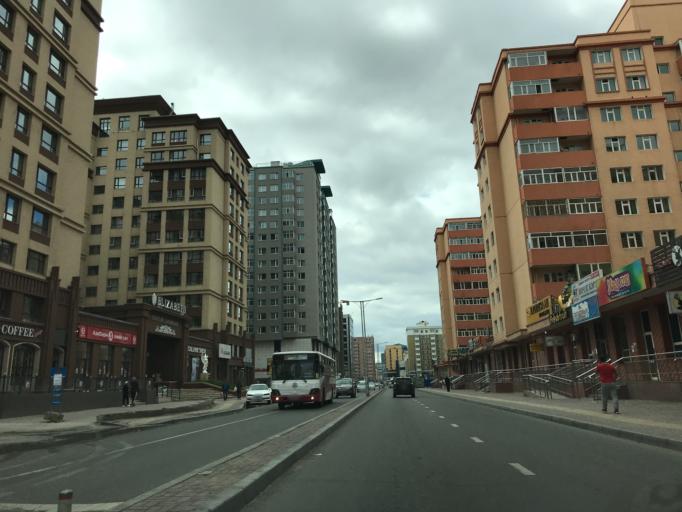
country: MN
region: Ulaanbaatar
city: Ulaanbaatar
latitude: 47.9046
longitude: 106.9340
